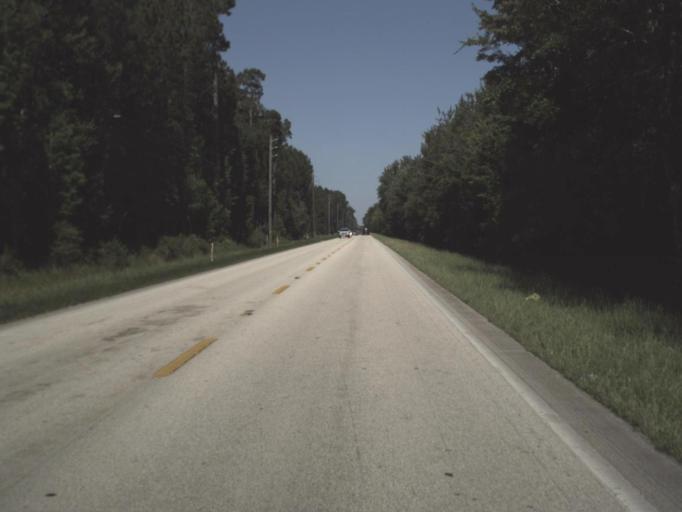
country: US
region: Florida
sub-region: Duval County
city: Baldwin
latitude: 30.3106
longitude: -81.8834
